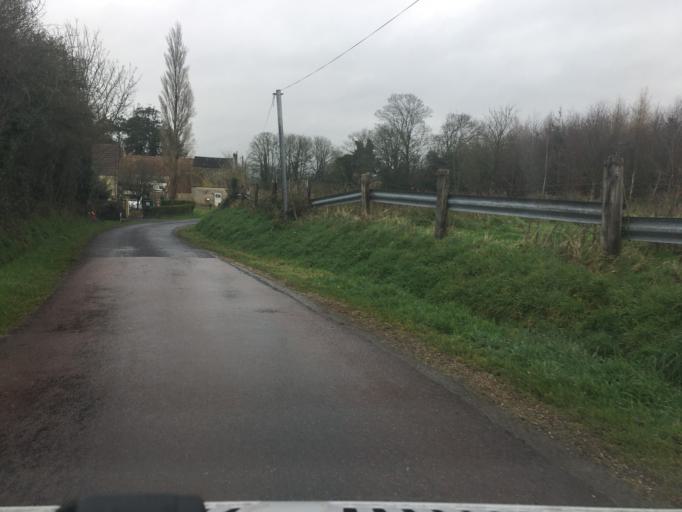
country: FR
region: Lower Normandy
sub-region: Departement de la Manche
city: Sainte-Mere-Eglise
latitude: 49.4258
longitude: -1.2642
